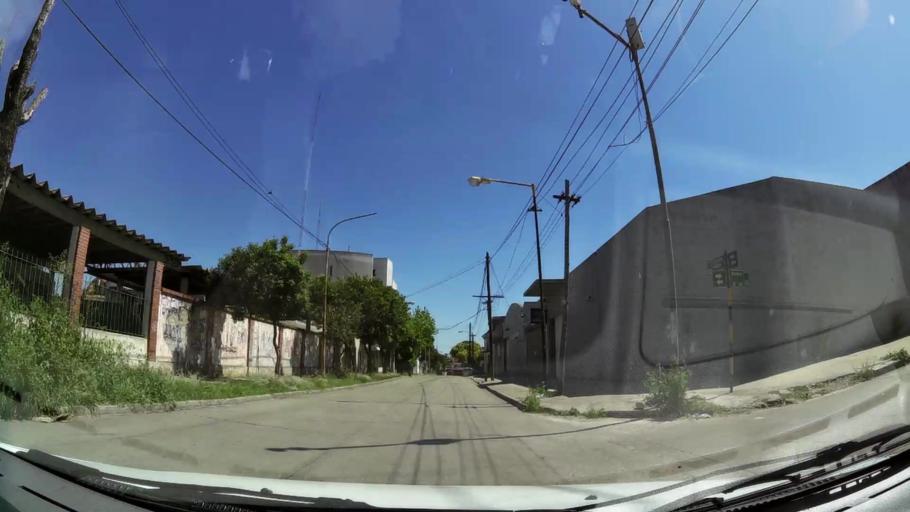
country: AR
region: Buenos Aires
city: Caseros
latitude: -34.5715
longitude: -58.5552
